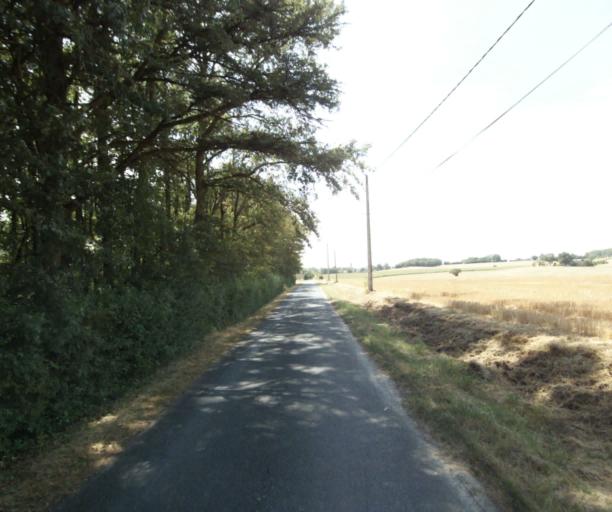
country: FR
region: Midi-Pyrenees
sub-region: Departement du Tarn
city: Puylaurens
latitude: 43.5257
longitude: 2.0226
